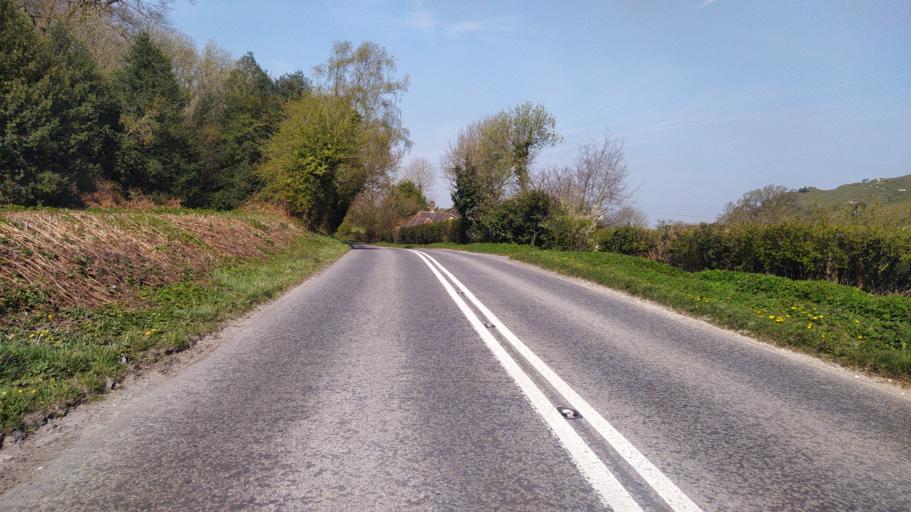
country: GB
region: England
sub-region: Wiltshire
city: Corsley
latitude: 51.1965
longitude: -2.2303
